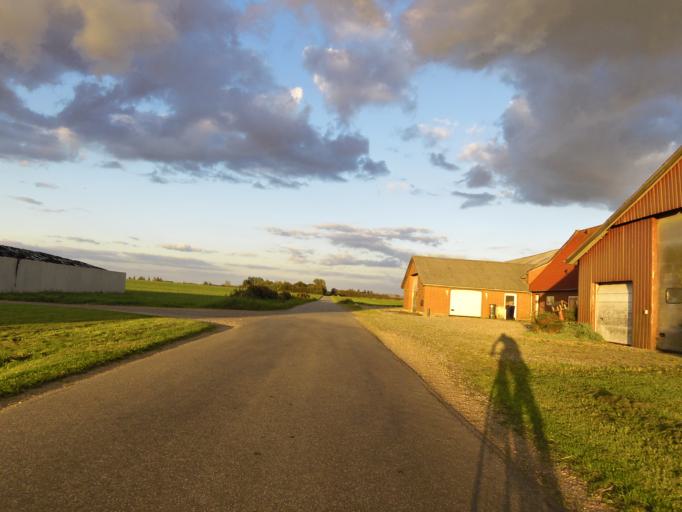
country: DK
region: South Denmark
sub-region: Tonder Kommune
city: Sherrebek
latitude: 55.2405
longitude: 8.8538
